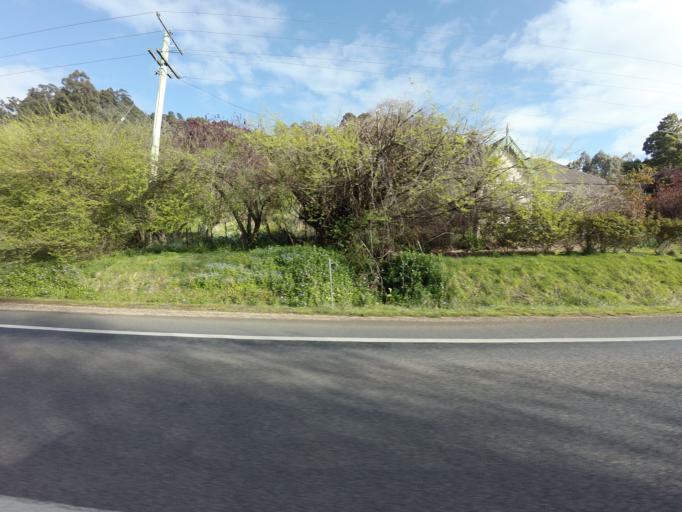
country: AU
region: Tasmania
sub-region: Huon Valley
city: Franklin
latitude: -43.0995
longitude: 147.0047
